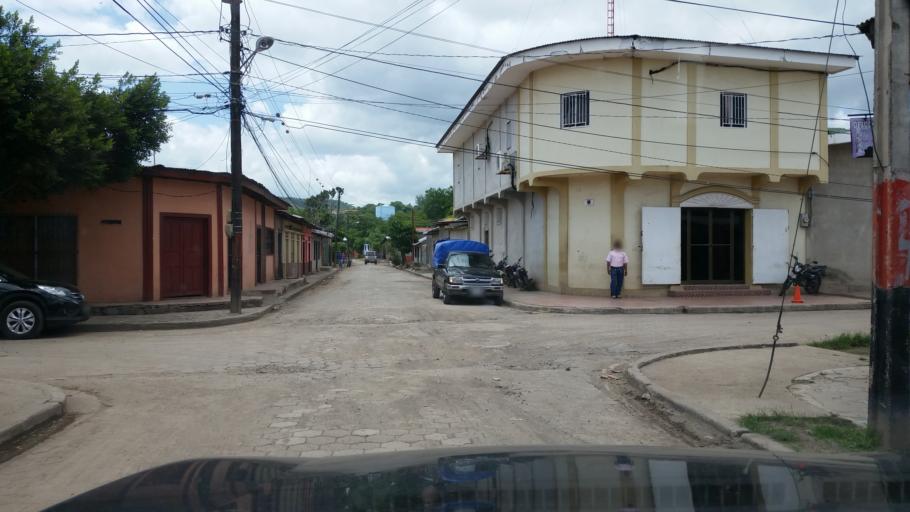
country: NI
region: Matagalpa
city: Ciudad Dario
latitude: 12.8492
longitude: -86.0981
